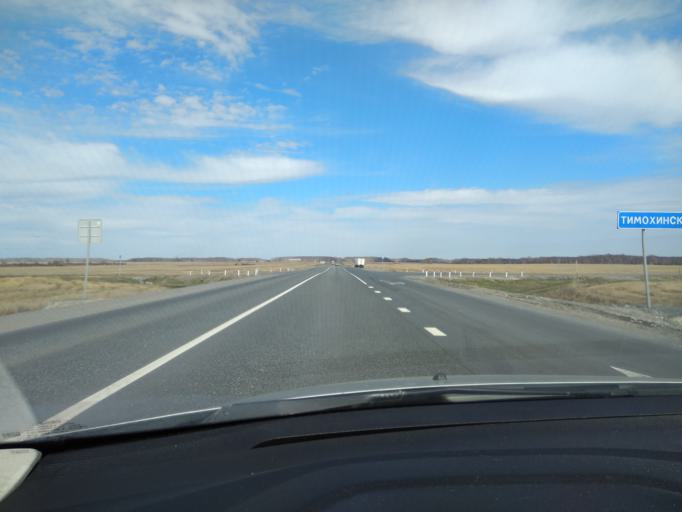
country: RU
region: Sverdlovsk
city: Pyshma
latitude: 56.9154
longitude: 63.1263
